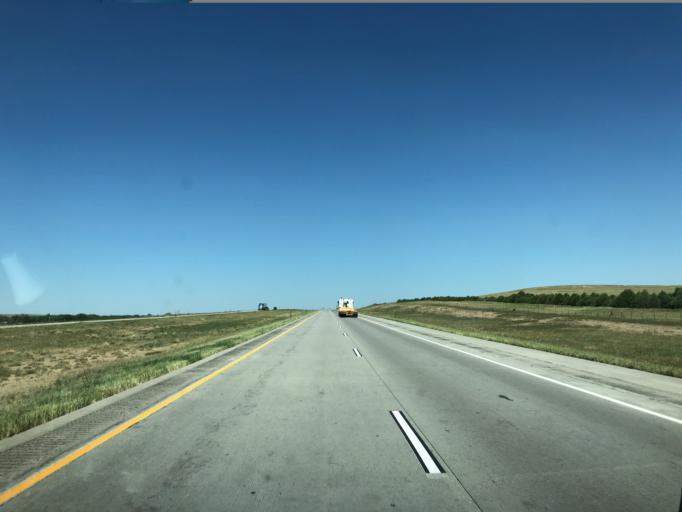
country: US
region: Colorado
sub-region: Lincoln County
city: Limon
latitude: 39.2796
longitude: -103.7626
